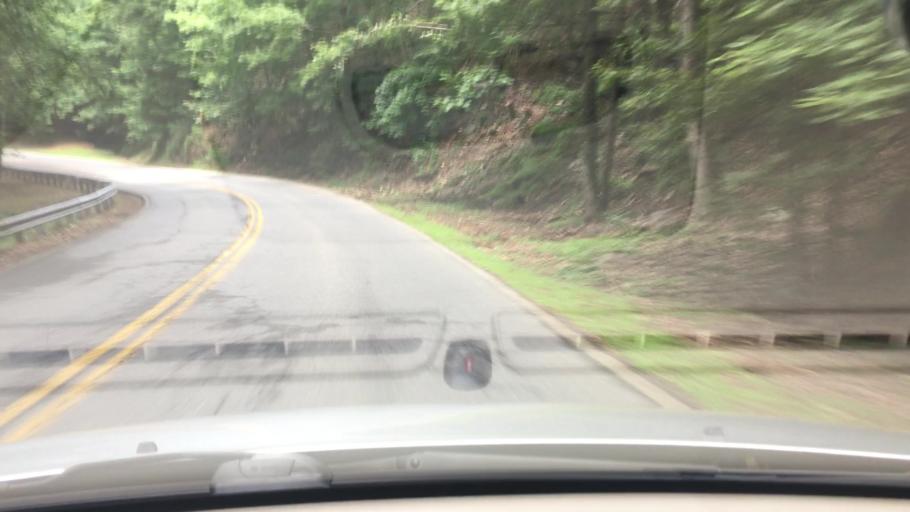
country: US
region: Georgia
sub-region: Dawson County
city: Dawsonville
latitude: 34.5646
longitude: -84.2519
